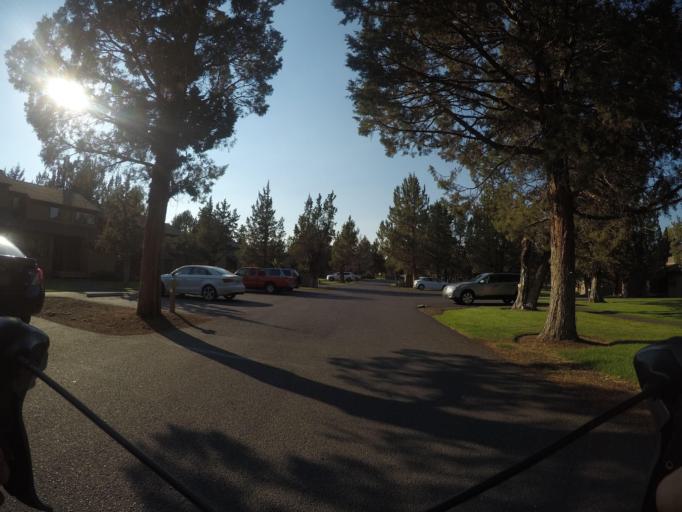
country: US
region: Oregon
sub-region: Deschutes County
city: Redmond
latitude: 44.2586
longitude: -121.2496
